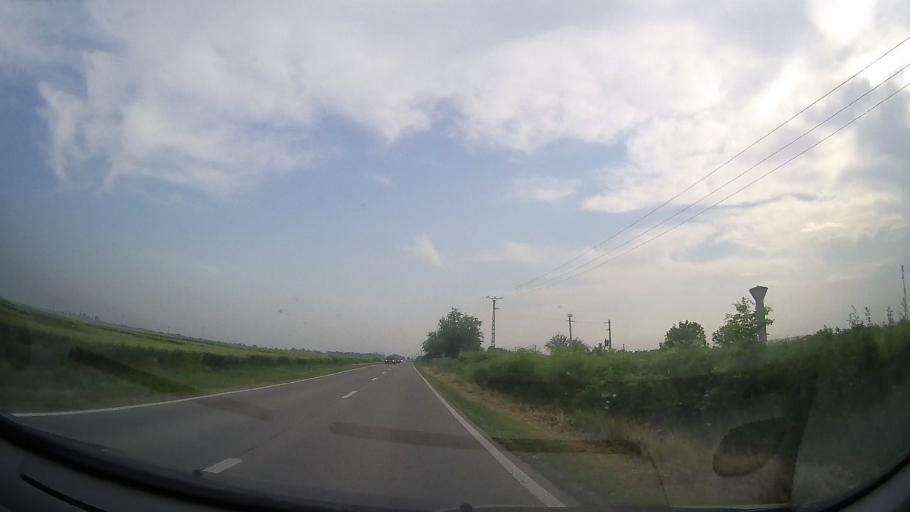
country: RO
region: Timis
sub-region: Comuna Parta
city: Parta
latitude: 45.6529
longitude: 21.1437
